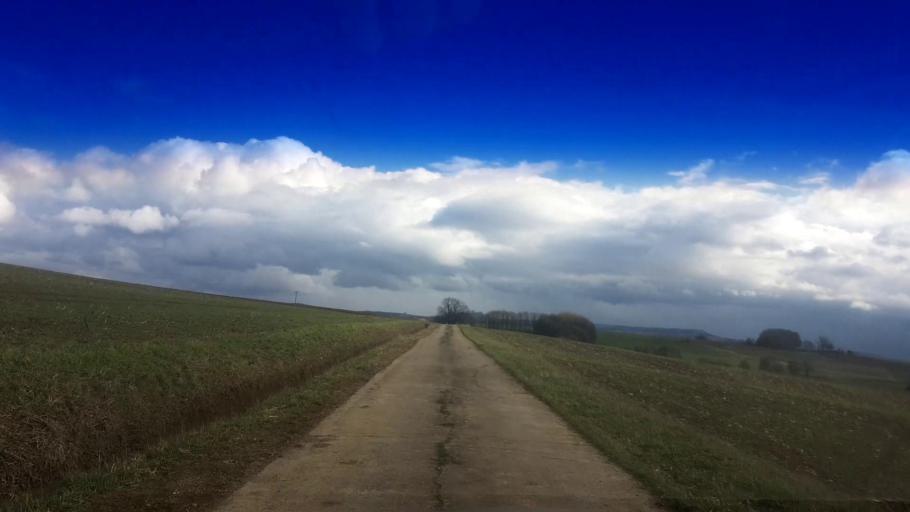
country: DE
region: Bavaria
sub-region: Upper Franconia
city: Schesslitz
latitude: 49.9944
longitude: 11.0154
